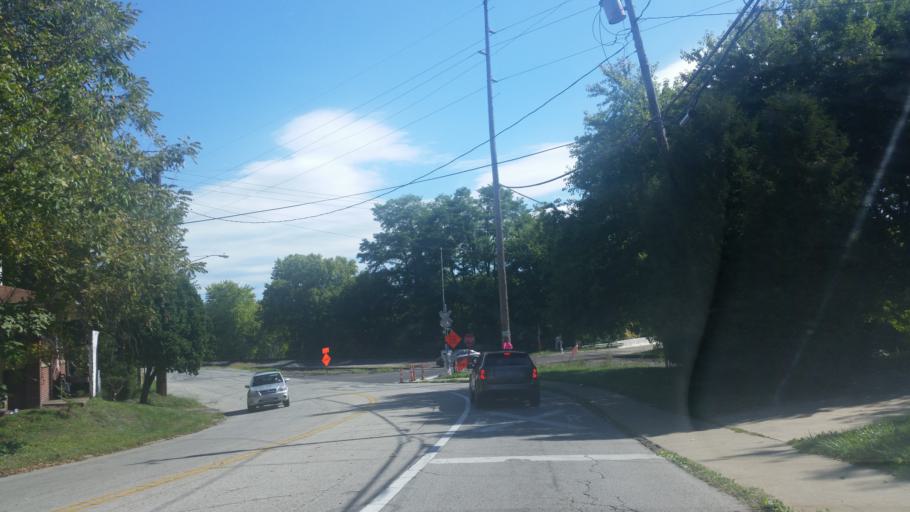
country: US
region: Ohio
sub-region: Summit County
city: Barberton
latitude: 41.0240
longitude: -81.5941
